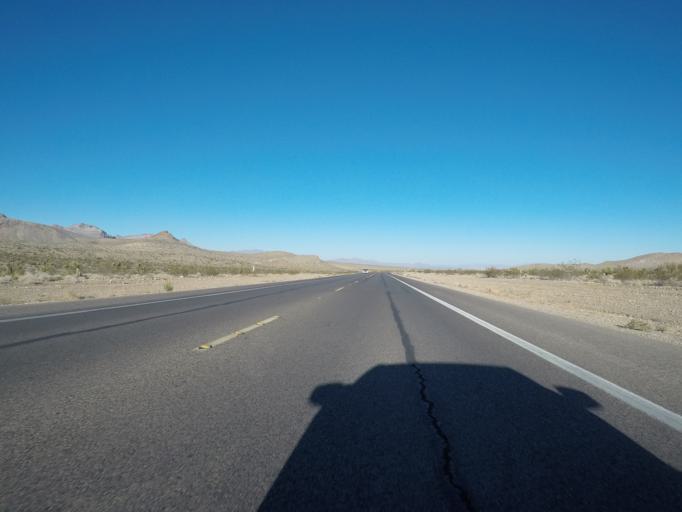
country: US
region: Nevada
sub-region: Clark County
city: Summerlin South
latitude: 36.1391
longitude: -115.4045
